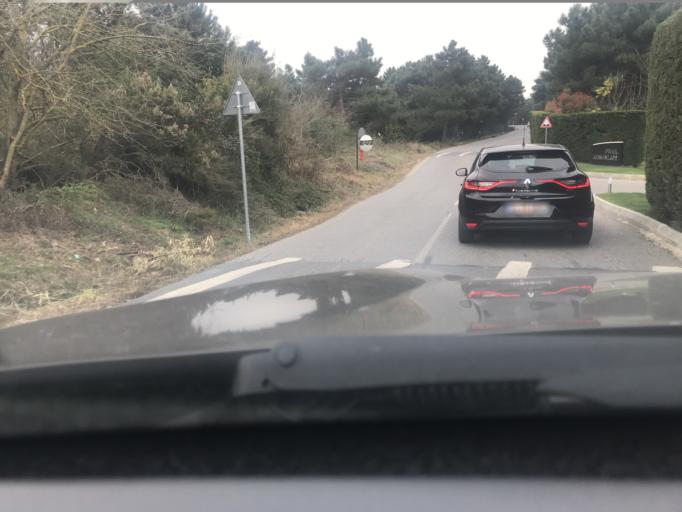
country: TR
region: Istanbul
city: Umraniye
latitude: 41.0444
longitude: 29.1702
